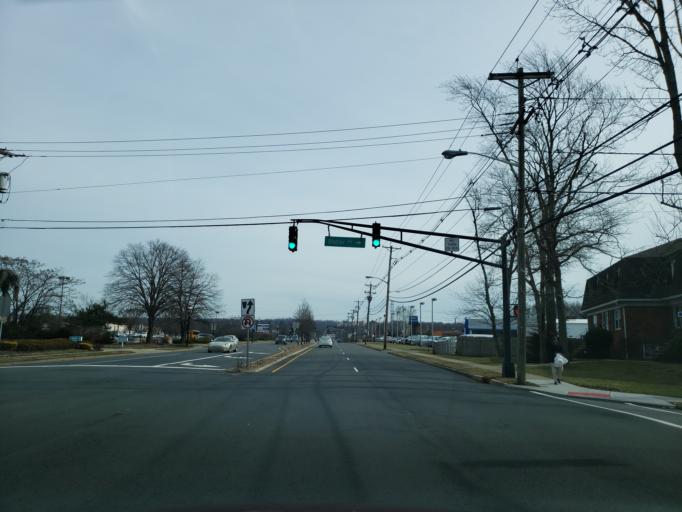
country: US
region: New Jersey
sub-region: Essex County
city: Westville
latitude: 40.8531
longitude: -74.3038
